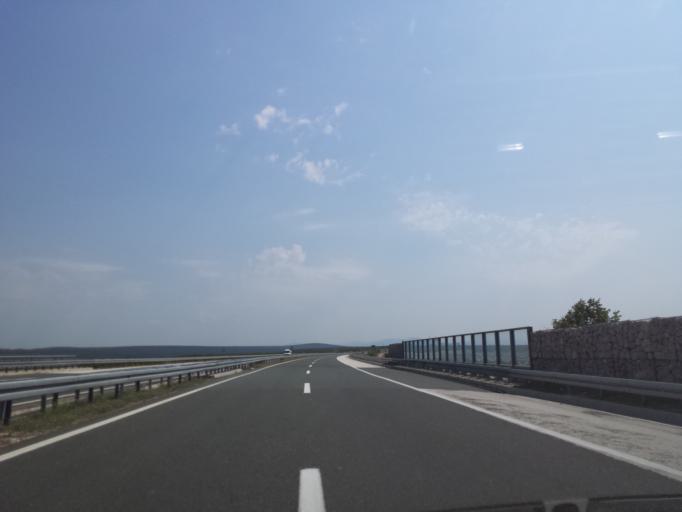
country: HR
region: Sibensko-Kniniska
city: Zaton
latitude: 43.8998
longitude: 15.7766
